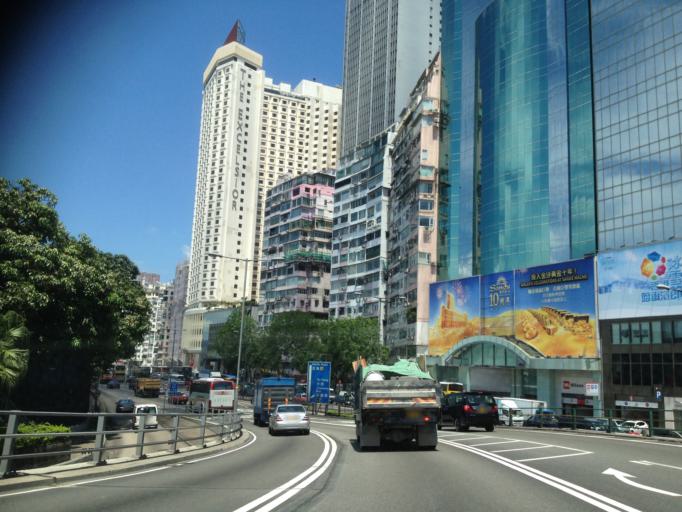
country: HK
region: Wanchai
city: Wan Chai
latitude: 22.2819
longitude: 114.1820
